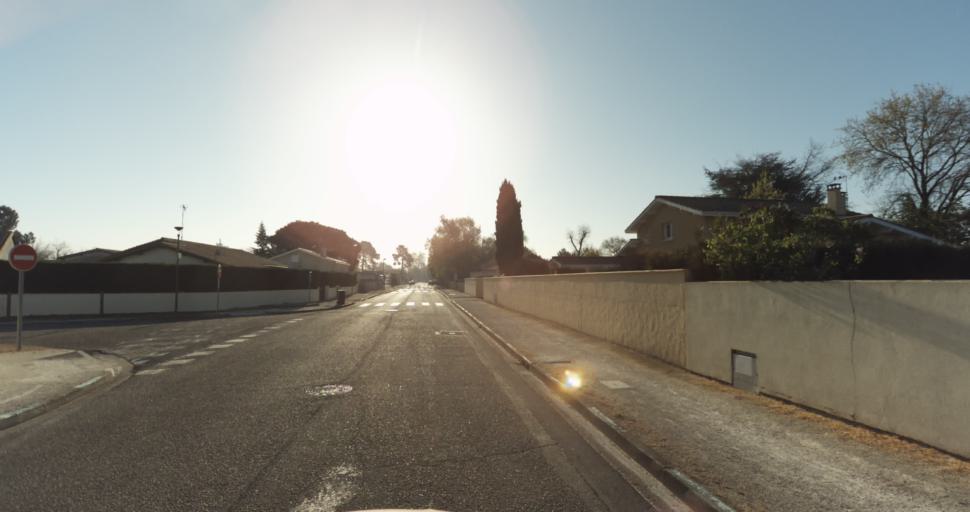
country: FR
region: Aquitaine
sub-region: Departement de la Gironde
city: Martignas-sur-Jalle
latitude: 44.8129
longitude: -0.7852
